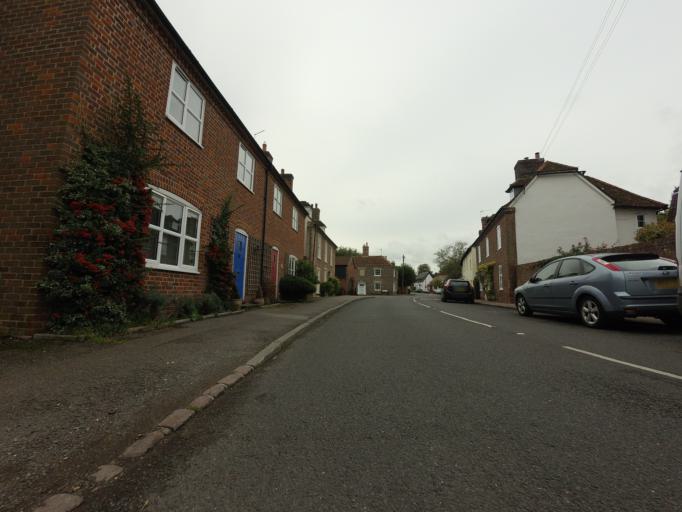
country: GB
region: England
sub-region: Hertfordshire
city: Reed
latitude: 52.0003
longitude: 0.0150
